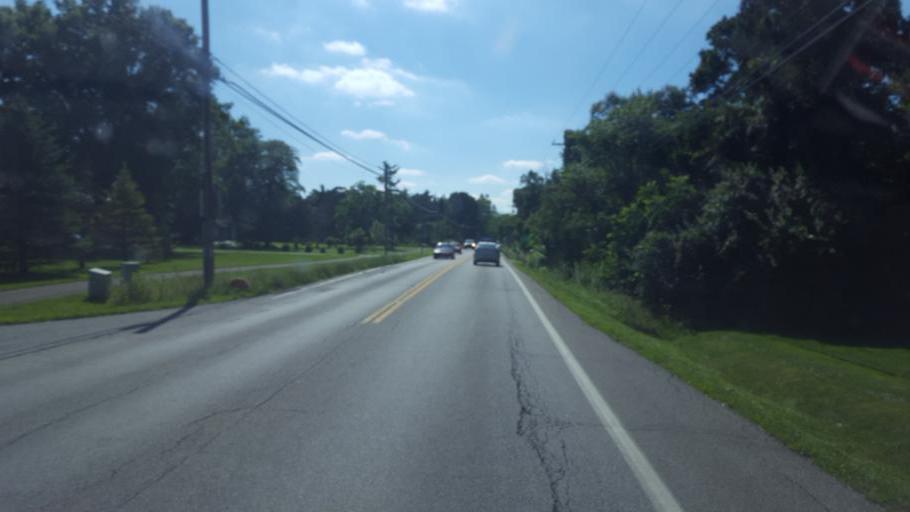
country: US
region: Ohio
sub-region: Franklin County
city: Worthington
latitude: 40.0896
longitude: -83.0407
